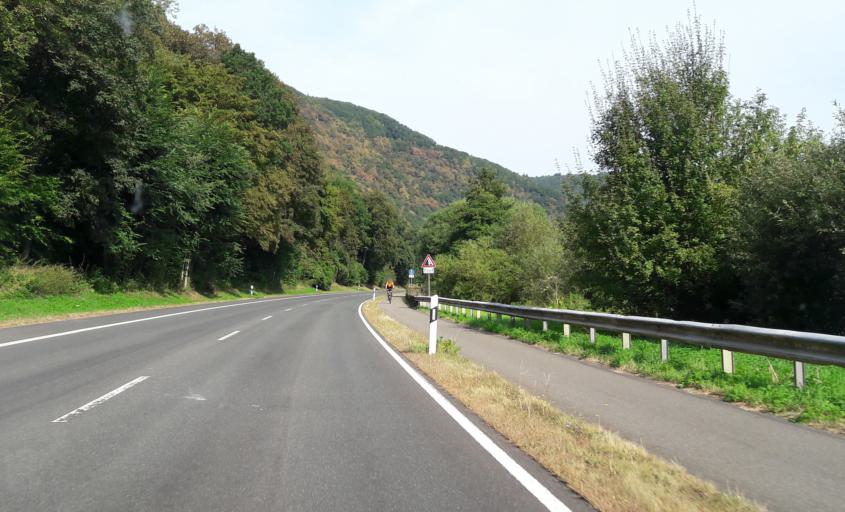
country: DE
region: Rheinland-Pfalz
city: Mesenich
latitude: 50.0959
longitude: 7.1927
